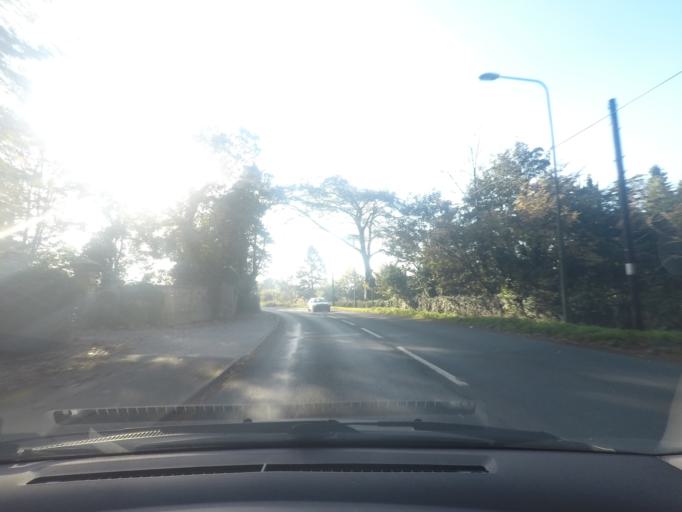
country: GB
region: England
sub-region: East Riding of Yorkshire
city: South Cave
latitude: 53.7649
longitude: -0.6004
